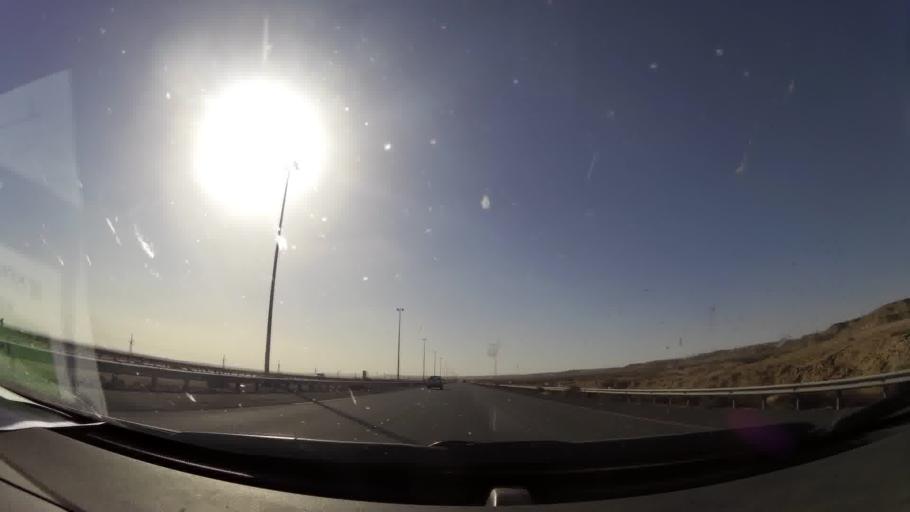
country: KW
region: Al Asimah
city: Kuwait City
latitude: 29.5416
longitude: 47.8540
